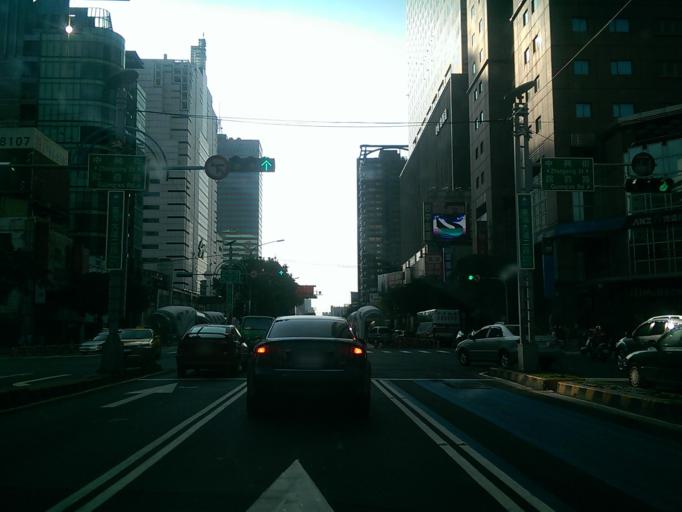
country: TW
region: Taiwan
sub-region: Taichung City
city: Taichung
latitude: 24.1548
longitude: 120.6642
